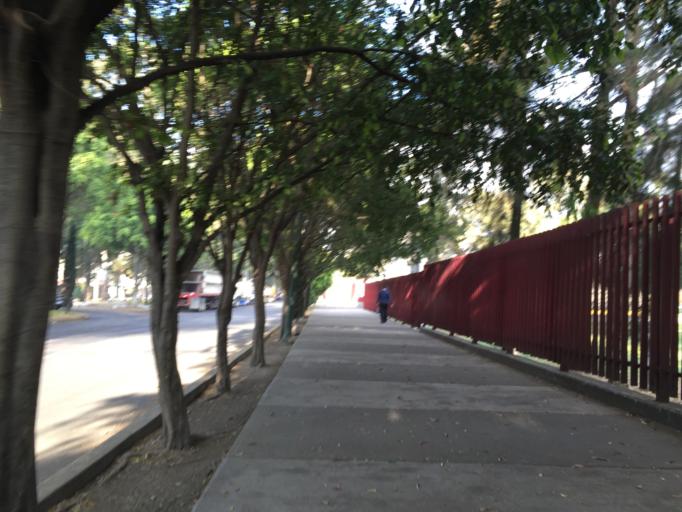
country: MX
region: Mexico
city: Colonia Lindavista
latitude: 19.4966
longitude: -99.1409
